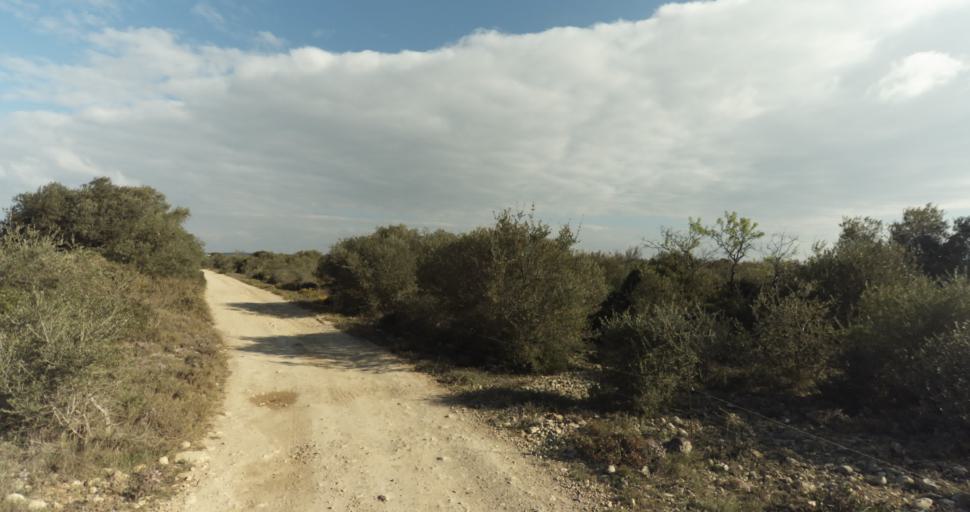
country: FR
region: Languedoc-Roussillon
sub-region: Departement de l'Aude
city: Leucate
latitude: 42.9382
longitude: 3.0122
